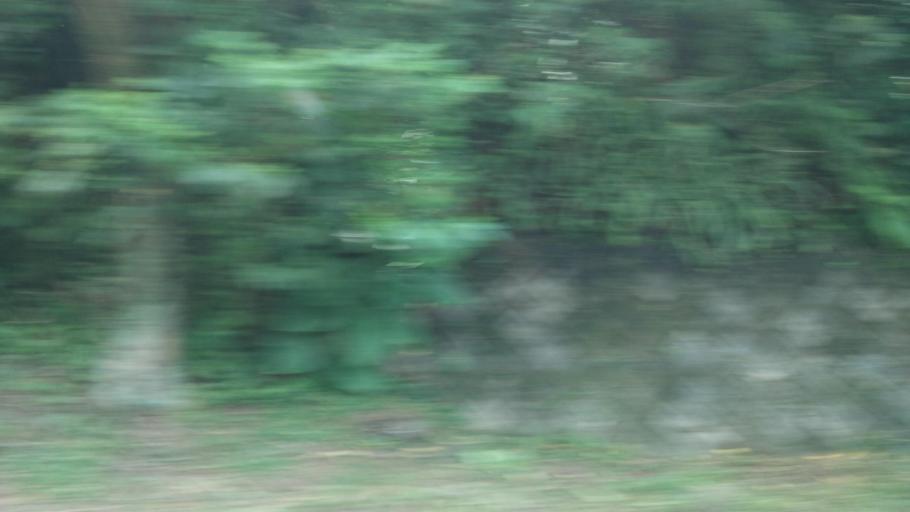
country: TW
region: Taipei
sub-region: Taipei
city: Banqiao
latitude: 24.9373
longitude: 121.4620
